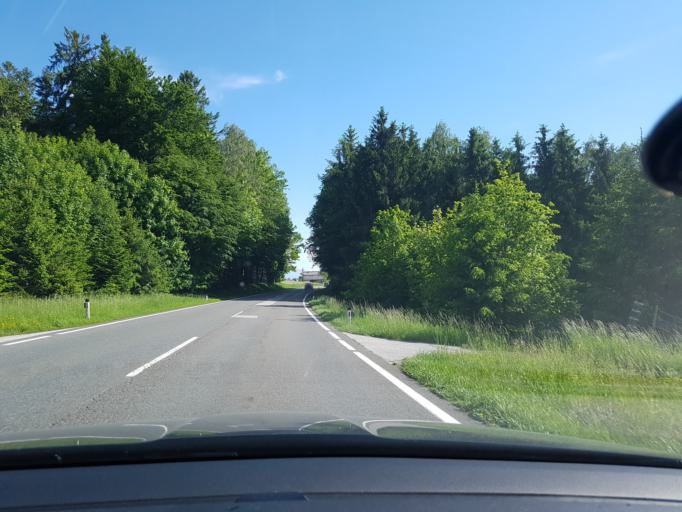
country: AT
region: Salzburg
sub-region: Politischer Bezirk Salzburg-Umgebung
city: Obertrum am See
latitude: 47.9141
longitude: 13.0826
